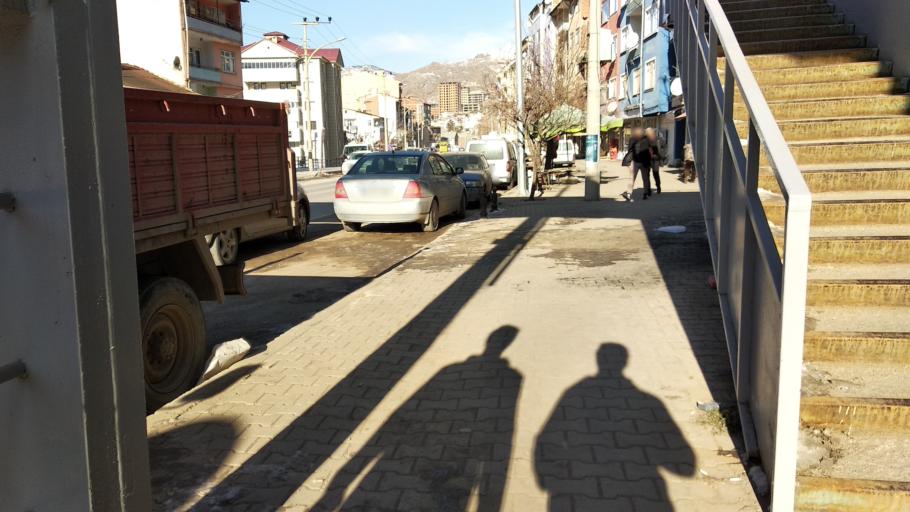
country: TR
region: Gumushane
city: Gumushkhane
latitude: 40.4544
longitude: 39.4924
